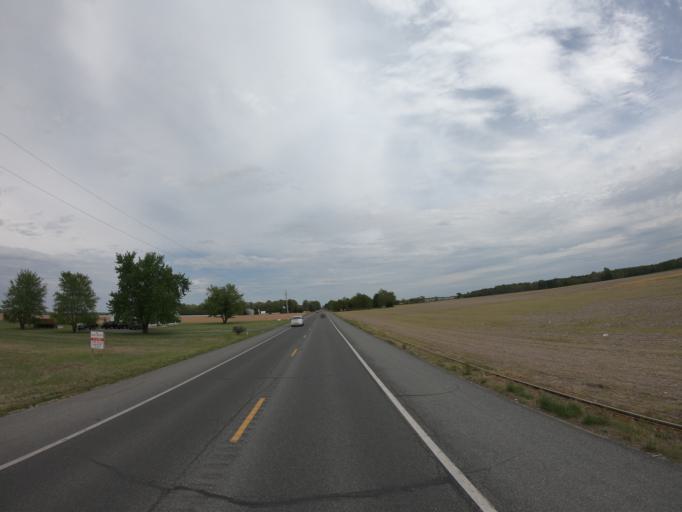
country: US
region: Delaware
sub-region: Sussex County
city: Milton
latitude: 38.7870
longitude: -75.3351
